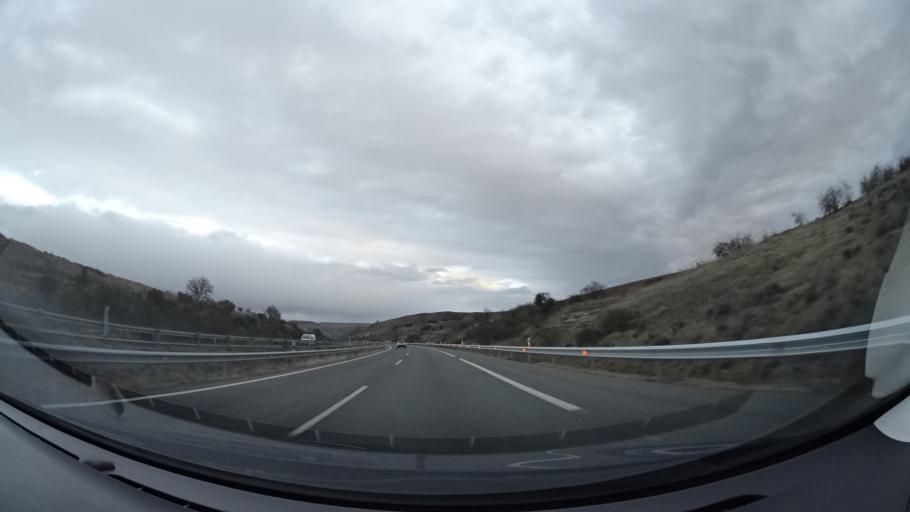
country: ES
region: La Rioja
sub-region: Provincia de La Rioja
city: Cenicero
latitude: 42.4614
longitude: -2.6276
